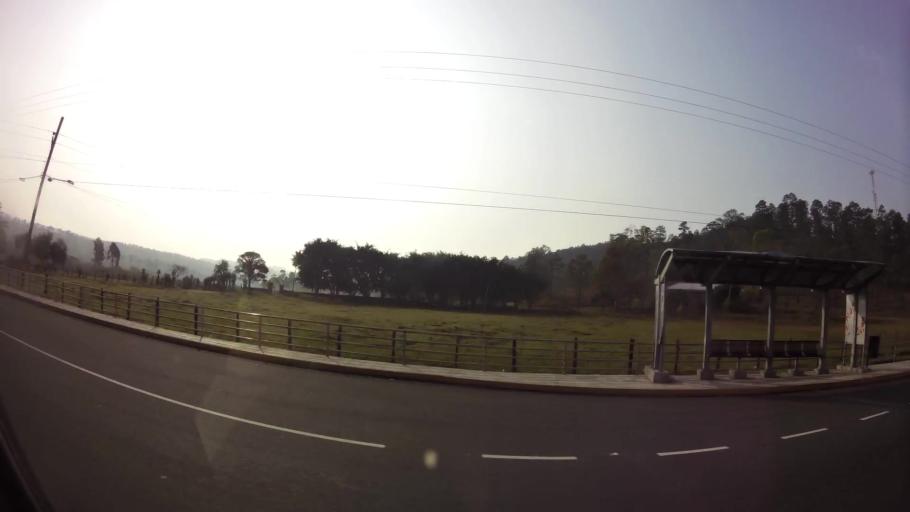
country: HN
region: Francisco Morazan
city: Zambrano
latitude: 14.2787
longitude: -87.4044
